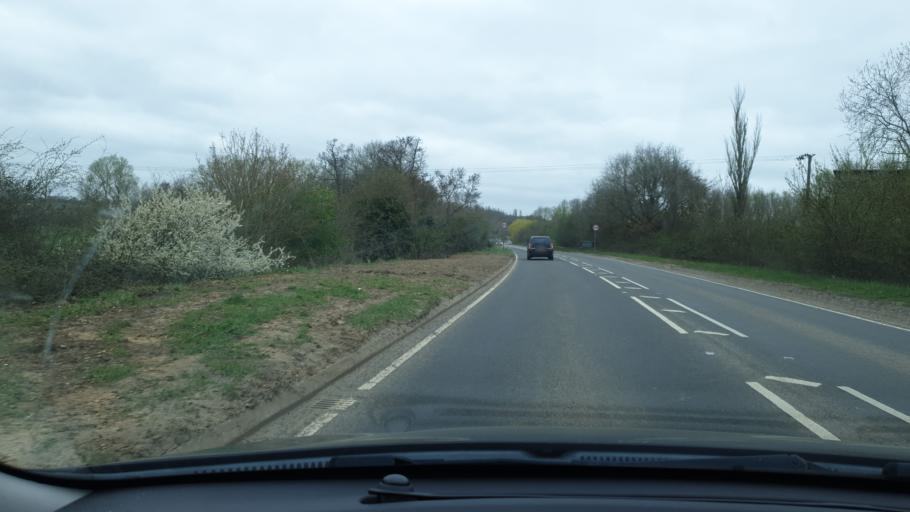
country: GB
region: England
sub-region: Essex
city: Great Horkesley
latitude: 51.9677
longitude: 0.8674
